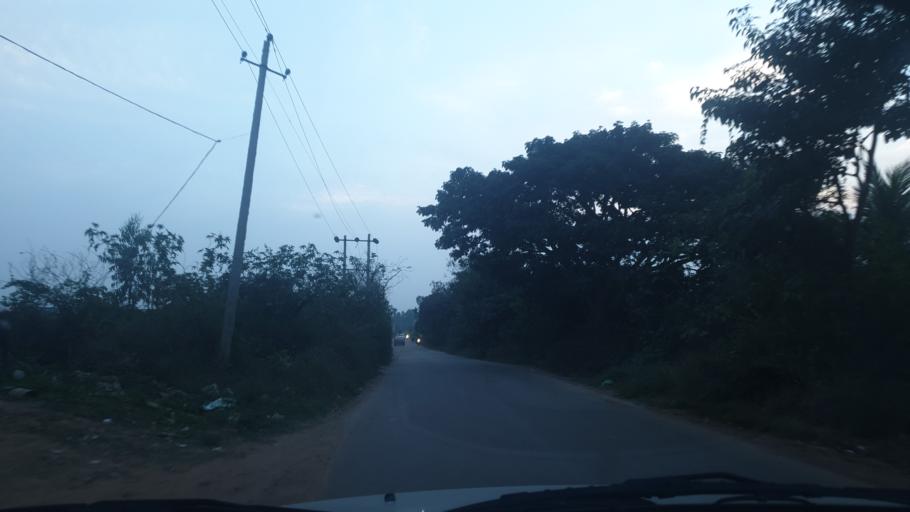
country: IN
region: Karnataka
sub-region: Bangalore Urban
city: Yelahanka
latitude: 13.0650
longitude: 77.6882
